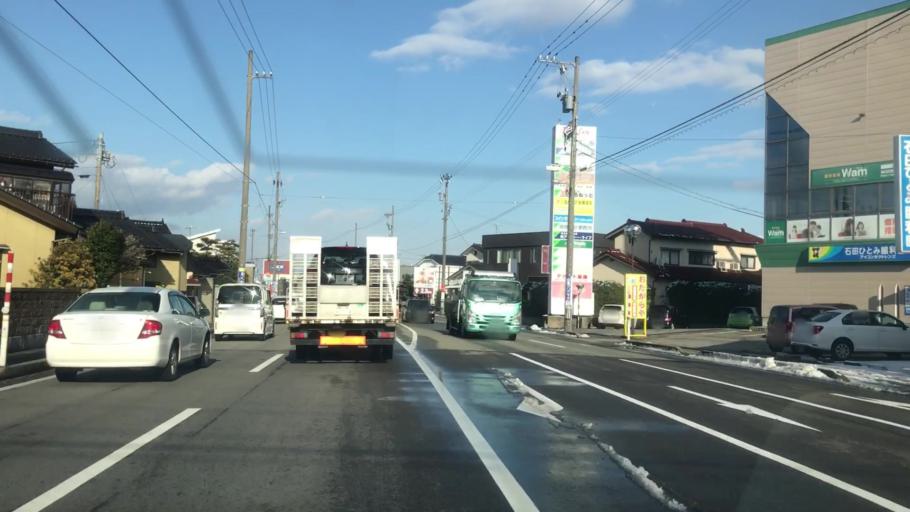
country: JP
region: Toyama
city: Toyama-shi
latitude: 36.6714
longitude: 137.2434
